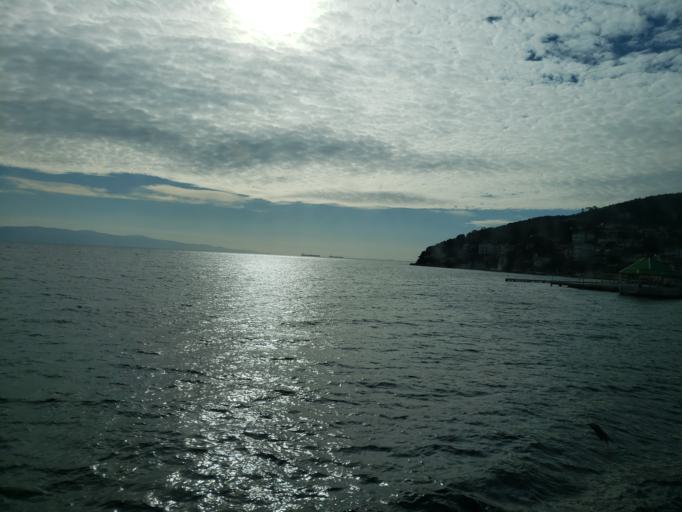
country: TR
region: Istanbul
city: Adalan
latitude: 40.8797
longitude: 29.0740
